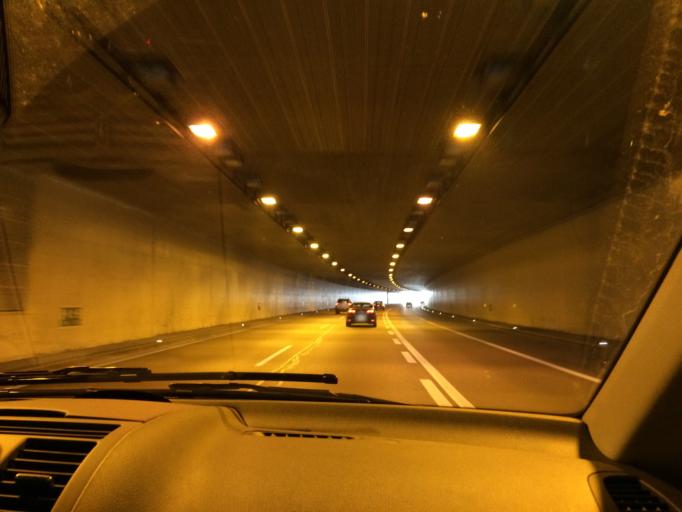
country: CH
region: Bern
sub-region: Emmental District
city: Kirchberg
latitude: 47.0863
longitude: 7.5739
